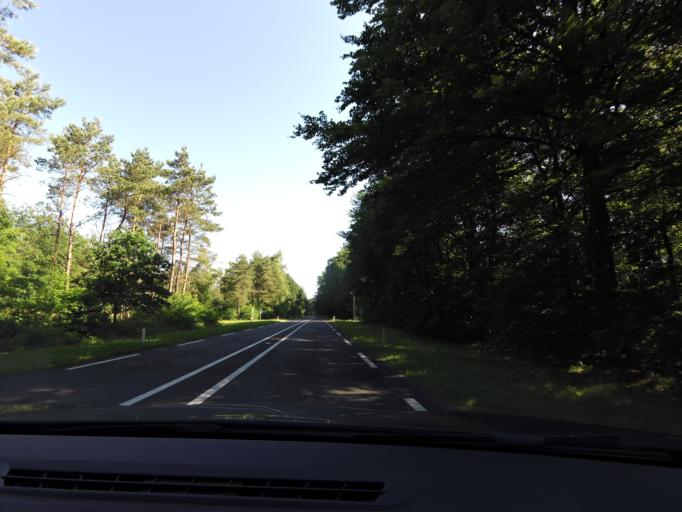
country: NL
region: Overijssel
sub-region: Gemeente Twenterand
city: Den Ham
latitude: 52.4754
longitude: 6.4272
